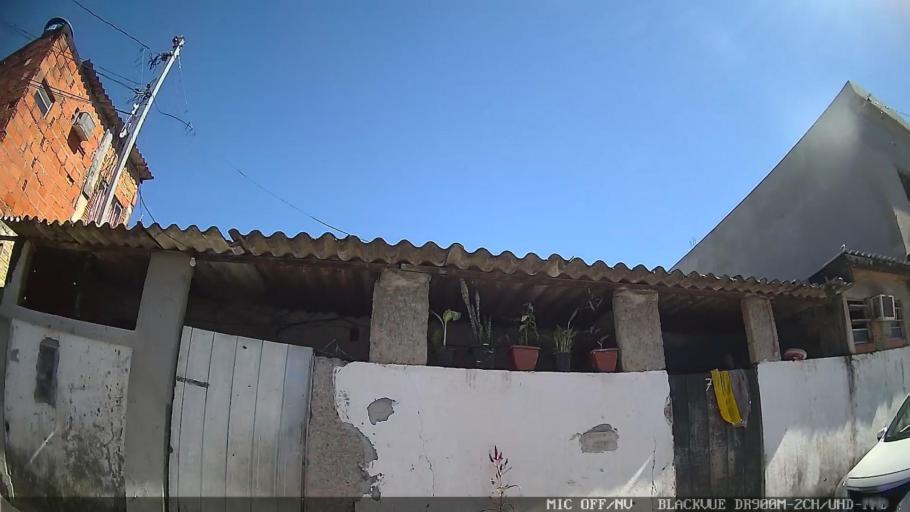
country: BR
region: Sao Paulo
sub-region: Santos
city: Santos
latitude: -23.9534
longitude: -46.2970
